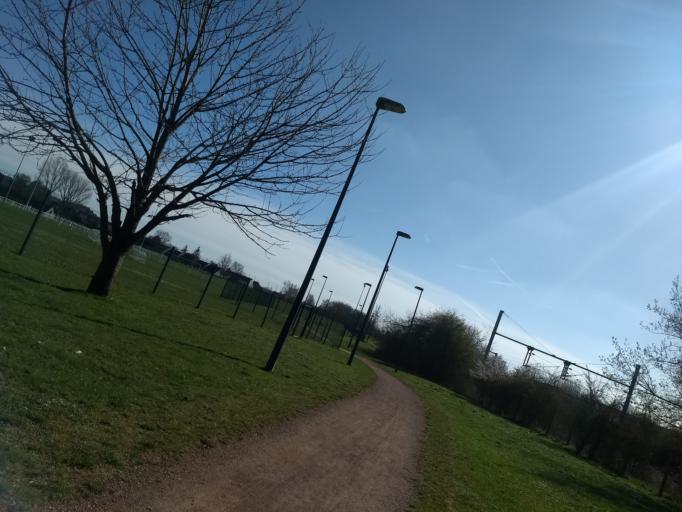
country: FR
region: Nord-Pas-de-Calais
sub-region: Departement du Pas-de-Calais
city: Achicourt
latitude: 50.2708
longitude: 2.7642
